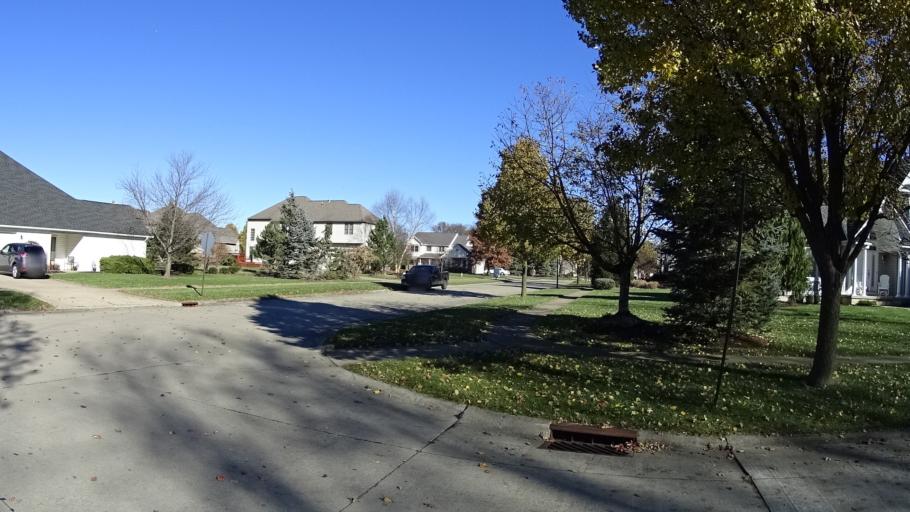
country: US
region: Ohio
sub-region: Lorain County
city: Elyria
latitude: 41.3436
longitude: -82.0862
